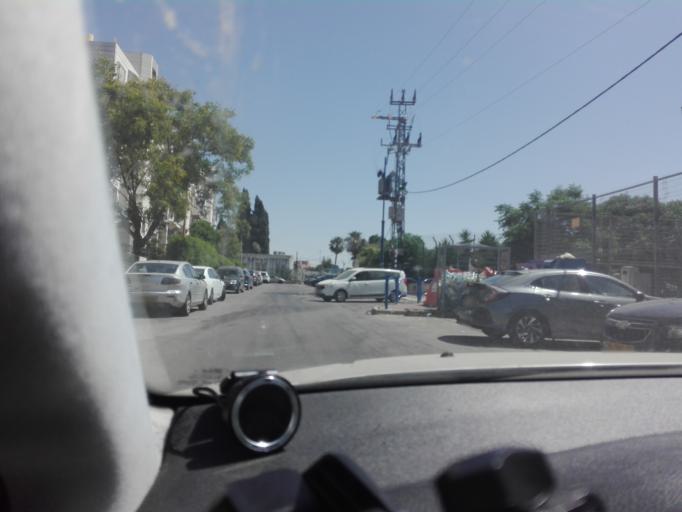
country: IL
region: Central District
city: Bene 'Ayish
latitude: 31.7332
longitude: 34.7392
